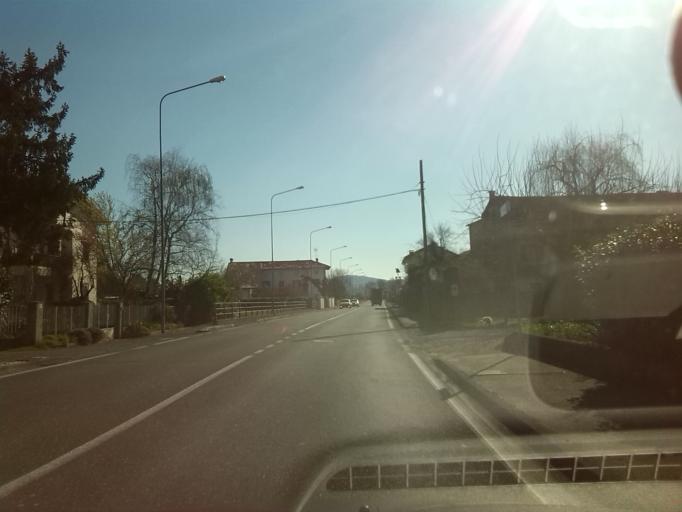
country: IT
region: Friuli Venezia Giulia
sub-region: Provincia di Udine
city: Remanzacco
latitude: 46.0862
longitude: 13.3302
